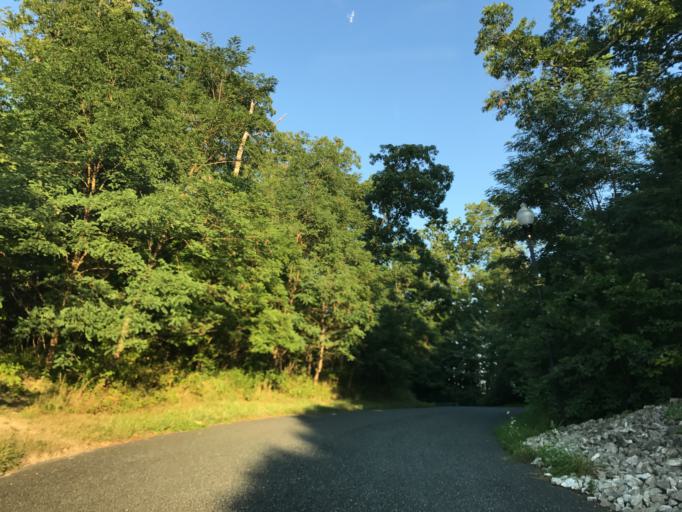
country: US
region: Maryland
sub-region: Baltimore County
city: White Marsh
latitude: 39.3867
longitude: -76.4500
